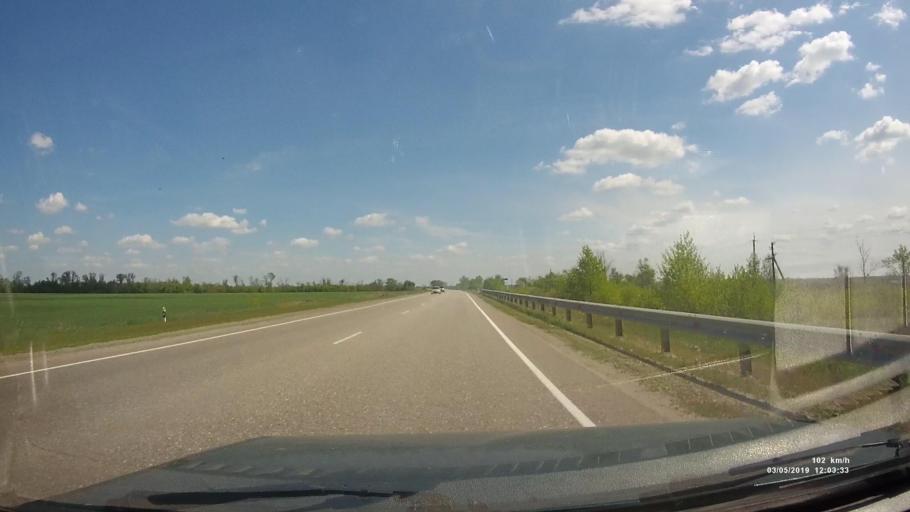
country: RU
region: Rostov
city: Bagayevskaya
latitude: 47.2739
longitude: 40.3926
